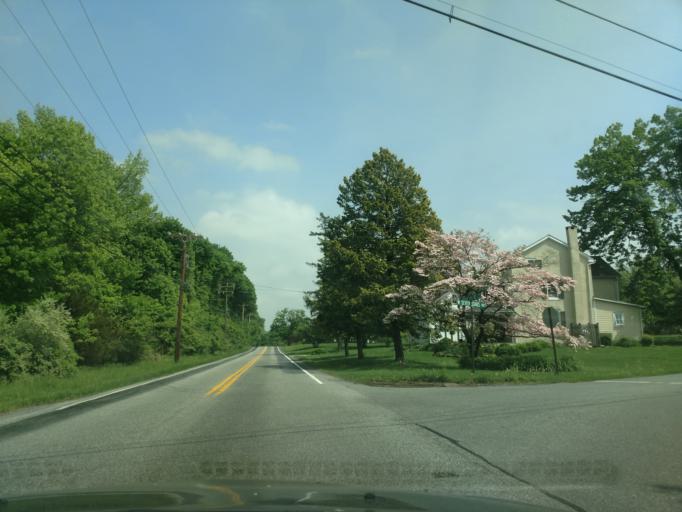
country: US
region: Pennsylvania
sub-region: Chester County
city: Spring City
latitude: 40.1638
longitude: -75.5949
